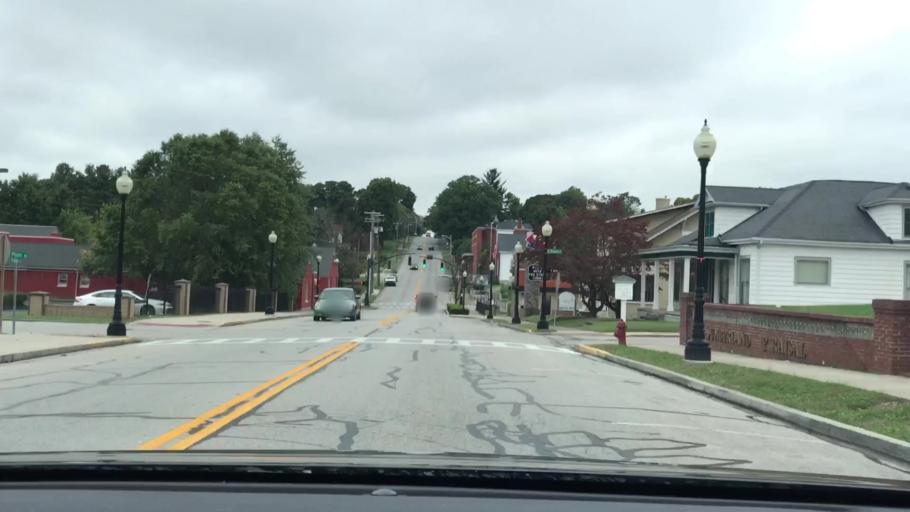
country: US
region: Kentucky
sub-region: Pulaski County
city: Somerset
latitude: 37.0942
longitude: -84.6054
